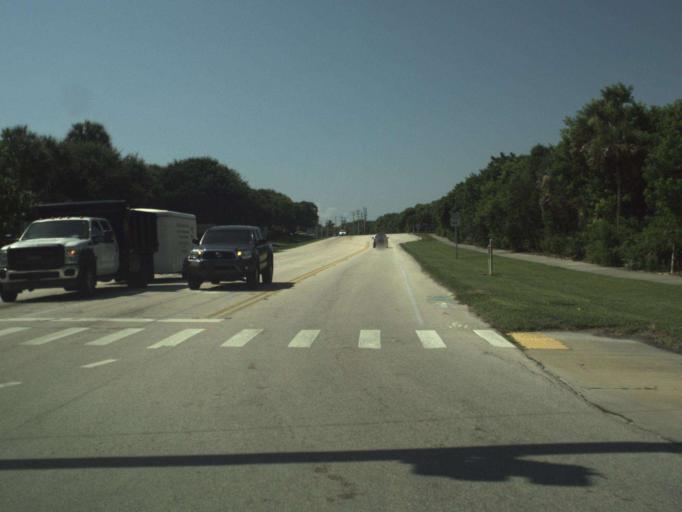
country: US
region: Florida
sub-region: Indian River County
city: Wabasso Beach
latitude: 27.7632
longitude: -80.3985
